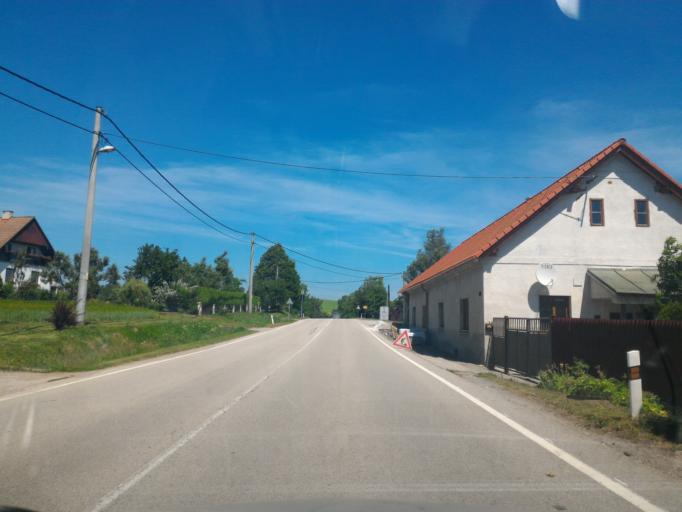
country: CZ
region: Vysocina
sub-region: Okres Jihlava
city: Trest'
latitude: 49.3228
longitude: 15.4825
